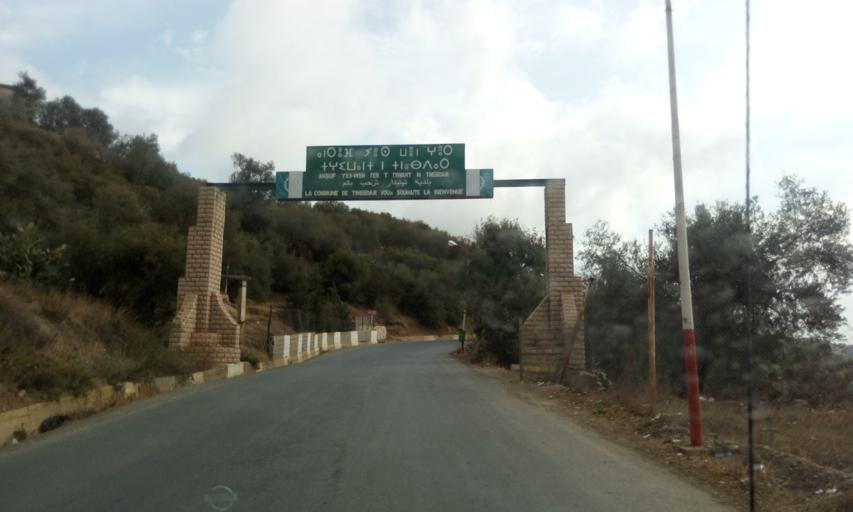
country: DZ
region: Tizi Ouzou
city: Chemini
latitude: 36.6213
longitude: 4.6630
